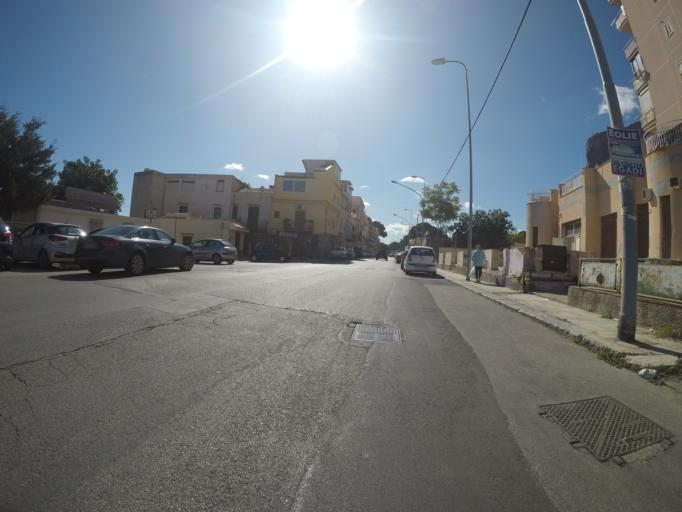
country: IT
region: Sicily
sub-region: Palermo
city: Palermo
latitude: 38.1651
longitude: 13.3692
